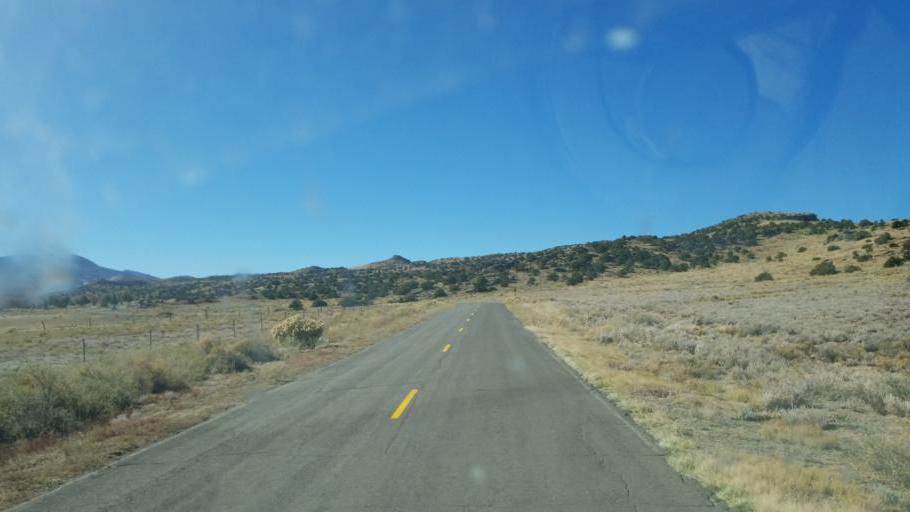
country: US
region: Colorado
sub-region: Rio Grande County
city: Del Norte
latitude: 37.6623
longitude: -106.3577
